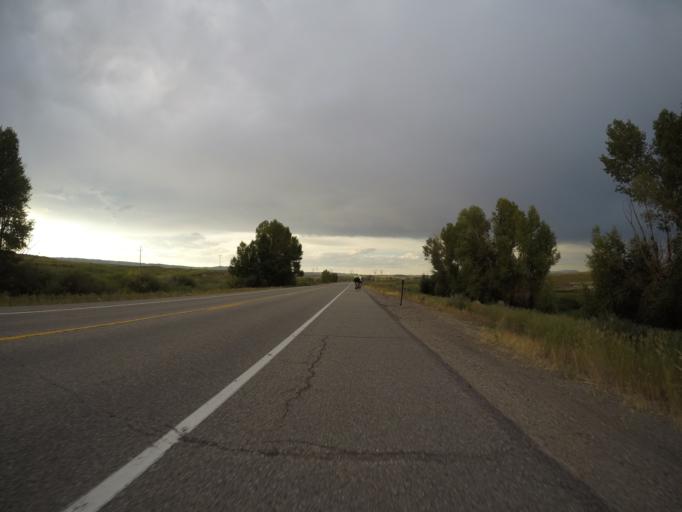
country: US
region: Idaho
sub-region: Bear Lake County
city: Montpelier
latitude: 42.0641
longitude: -110.9367
